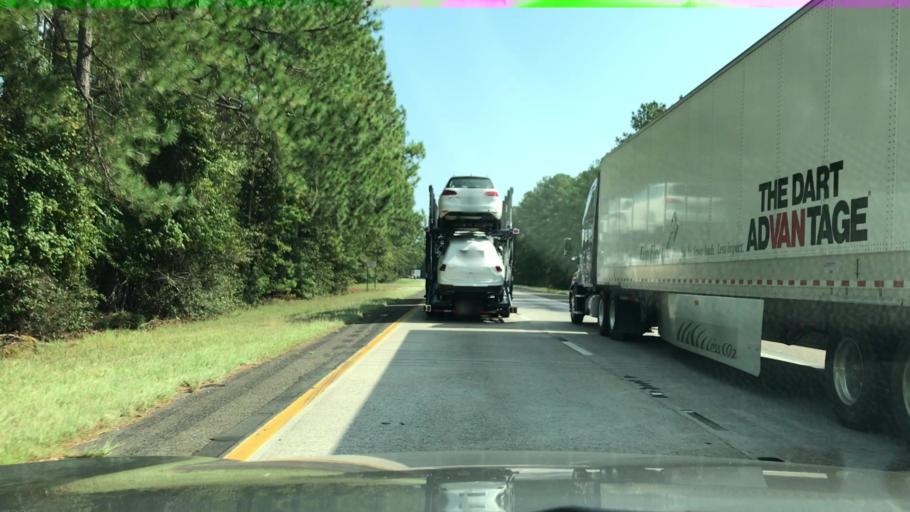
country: US
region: South Carolina
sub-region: Colleton County
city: Walterboro
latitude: 32.8217
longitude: -80.7532
